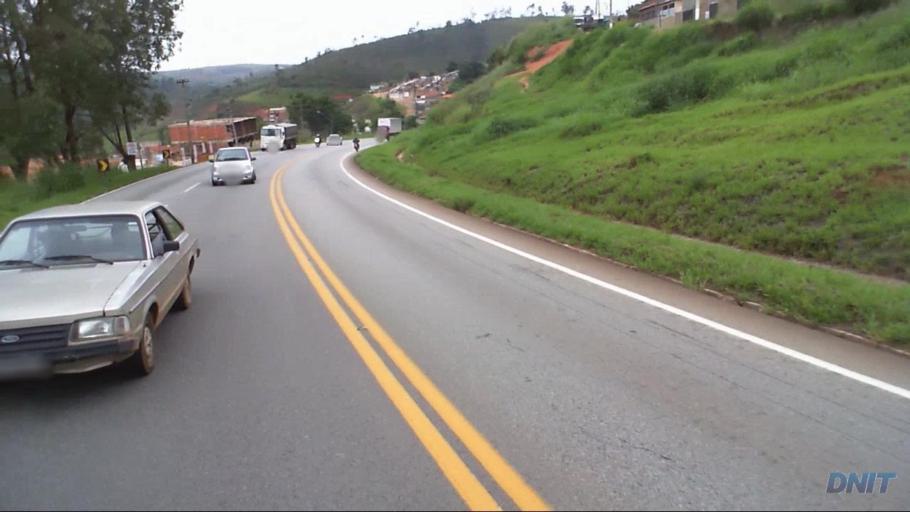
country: BR
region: Minas Gerais
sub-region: Joao Monlevade
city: Joao Monlevade
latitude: -19.8294
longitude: -43.0923
